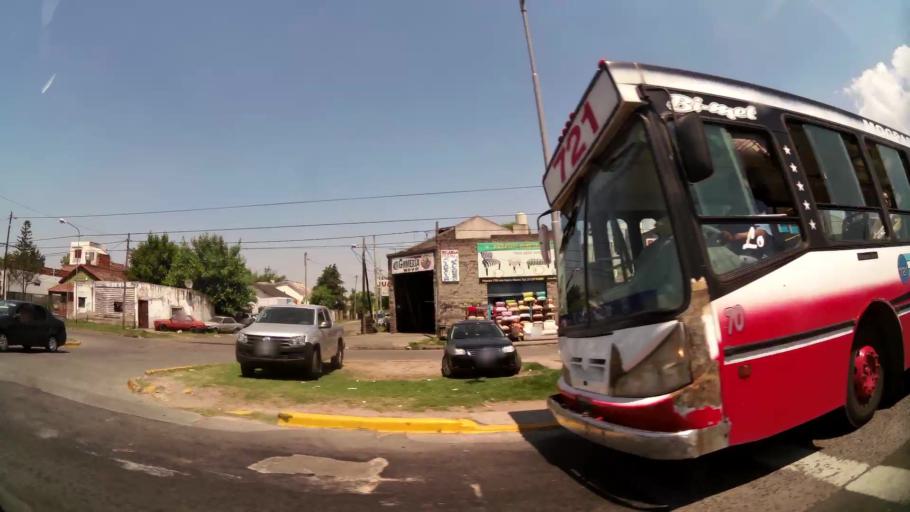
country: AR
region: Buenos Aires
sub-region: Partido de Tigre
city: Tigre
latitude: -34.4474
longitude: -58.6039
